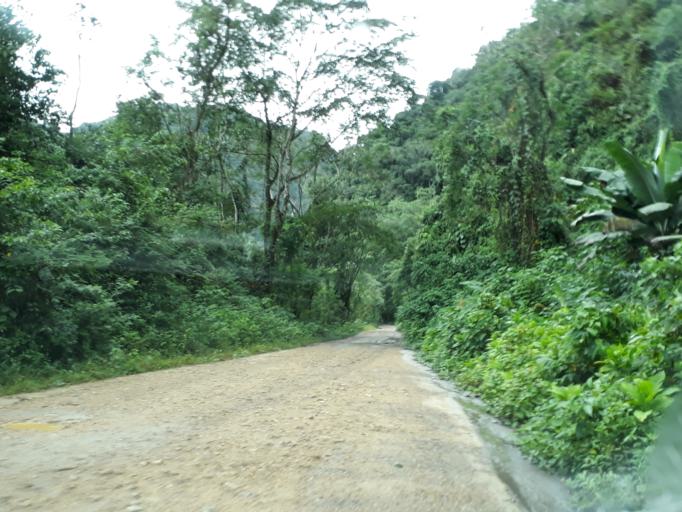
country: CO
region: Boyaca
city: Santa Maria
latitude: 4.7510
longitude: -73.3105
